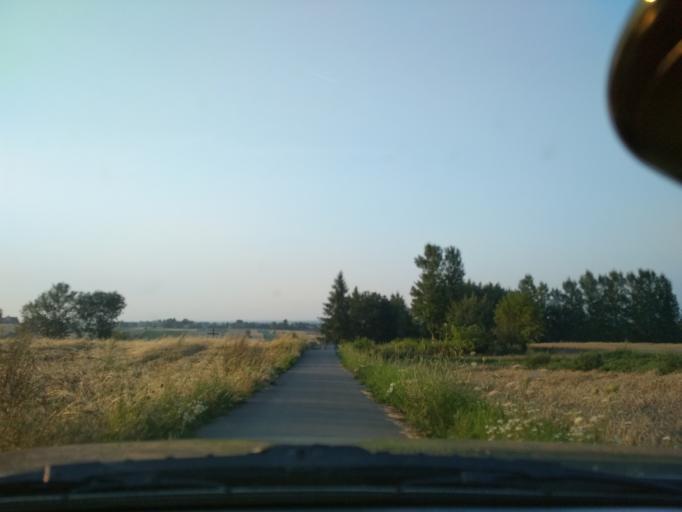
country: PL
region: Lesser Poland Voivodeship
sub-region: Powiat olkuski
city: Wolbrom
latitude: 50.4097
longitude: 19.8353
